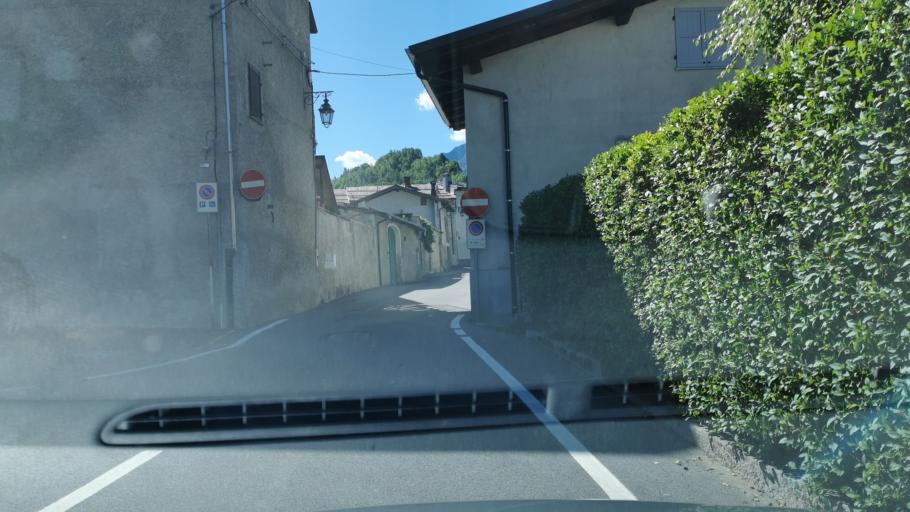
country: IT
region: Piedmont
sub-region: Provincia di Cuneo
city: Entracque
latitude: 44.2412
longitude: 7.4012
